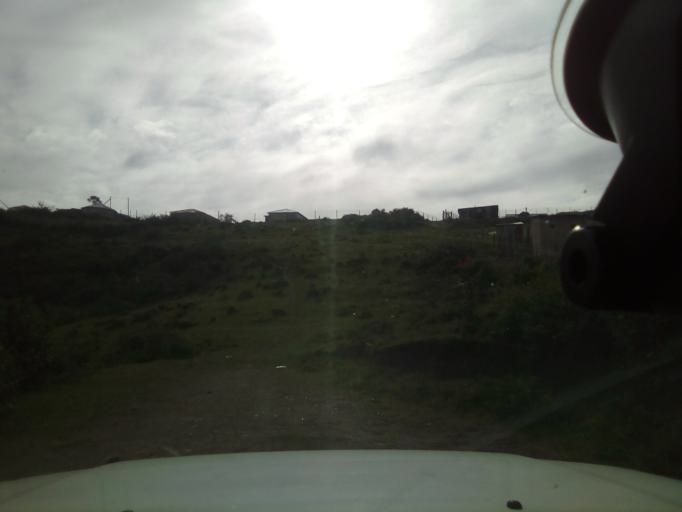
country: ZA
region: Eastern Cape
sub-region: Buffalo City Metropolitan Municipality
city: East London
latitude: -32.7954
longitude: 27.9673
